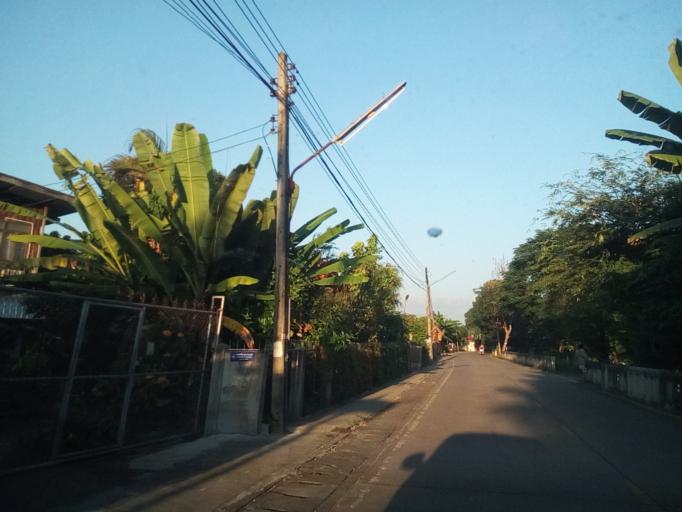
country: TH
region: Lamphun
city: Lamphun
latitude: 18.5819
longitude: 99.0119
